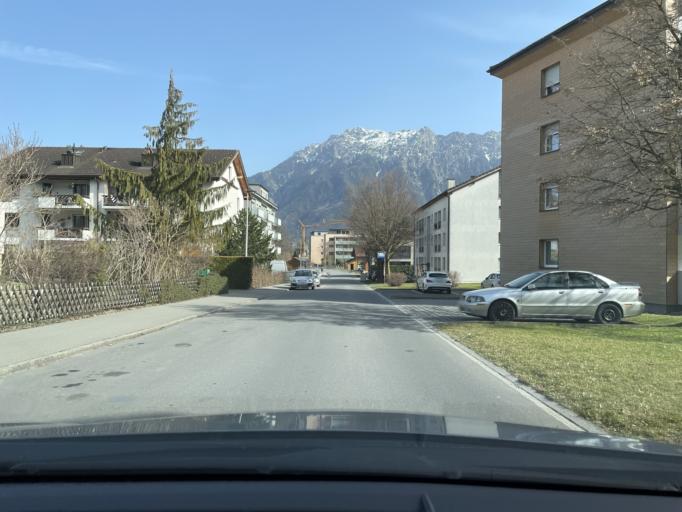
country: CH
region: Saint Gallen
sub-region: Wahlkreis Werdenberg
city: Buchs
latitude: 47.1572
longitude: 9.4747
